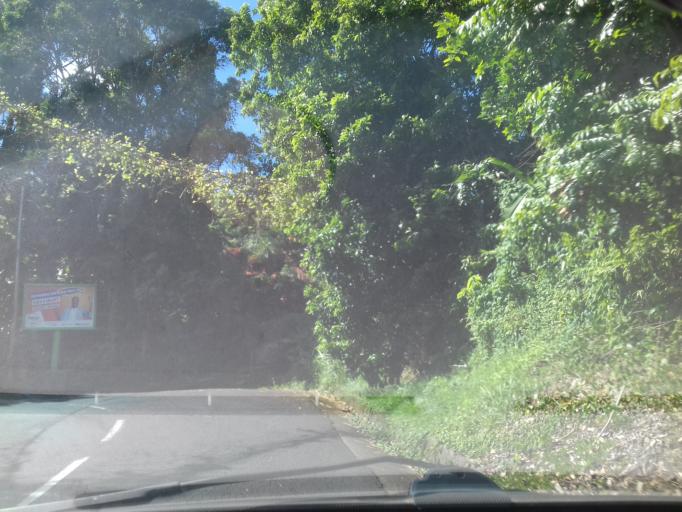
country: MQ
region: Martinique
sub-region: Martinique
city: Saint-Joseph
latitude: 14.6435
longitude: -61.0531
